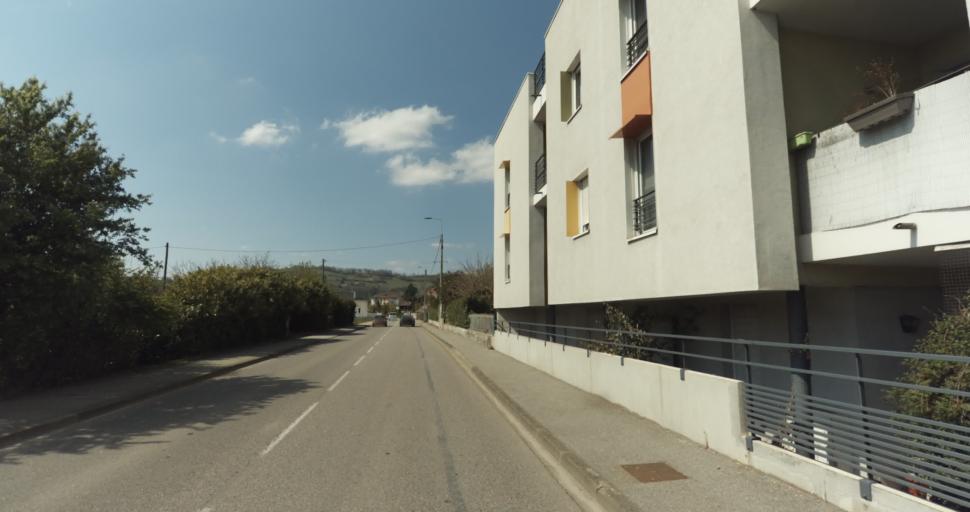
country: FR
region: Rhone-Alpes
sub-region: Departement de l'Isere
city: Saint-Marcellin
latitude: 45.1475
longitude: 5.3236
